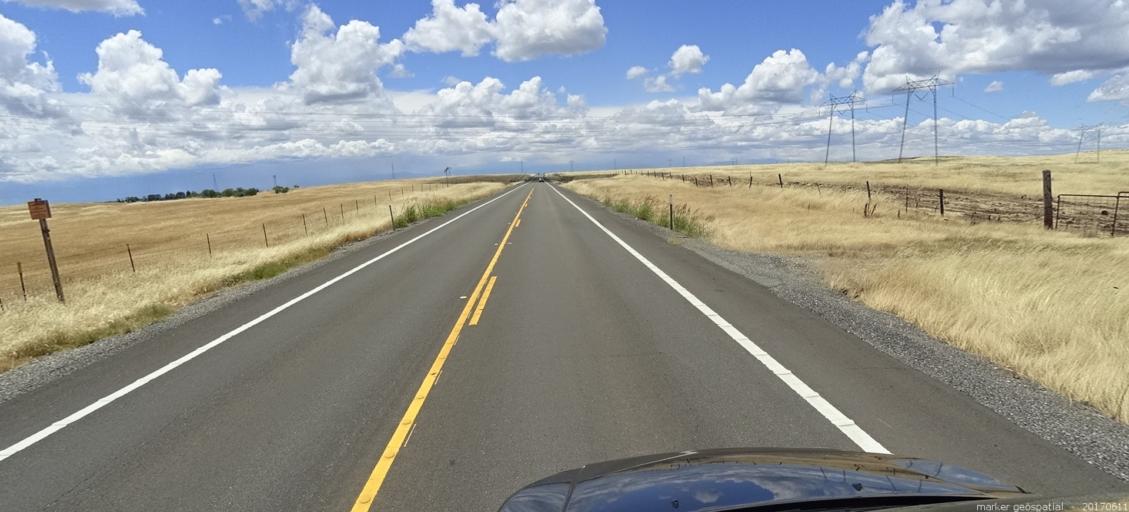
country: US
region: California
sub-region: Butte County
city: Durham
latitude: 39.6394
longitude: -121.6885
